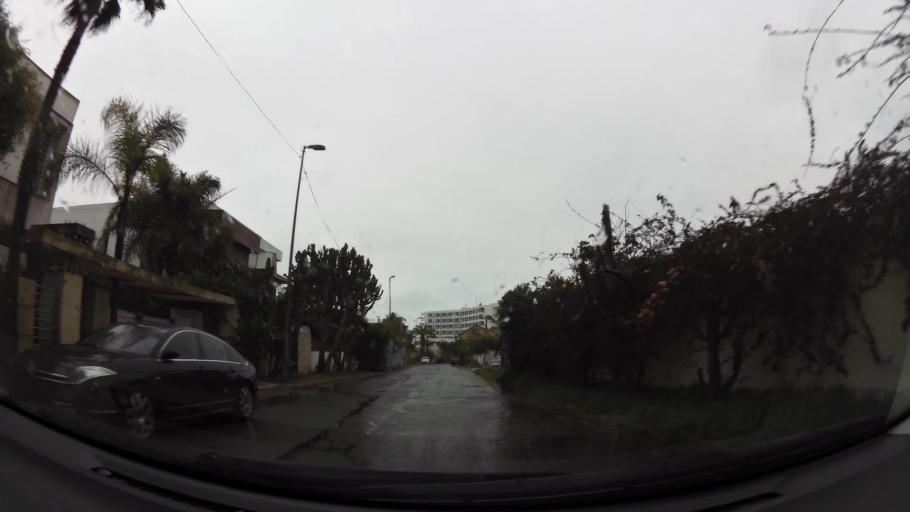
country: MA
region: Grand Casablanca
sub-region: Casablanca
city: Casablanca
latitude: 33.5897
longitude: -7.6753
